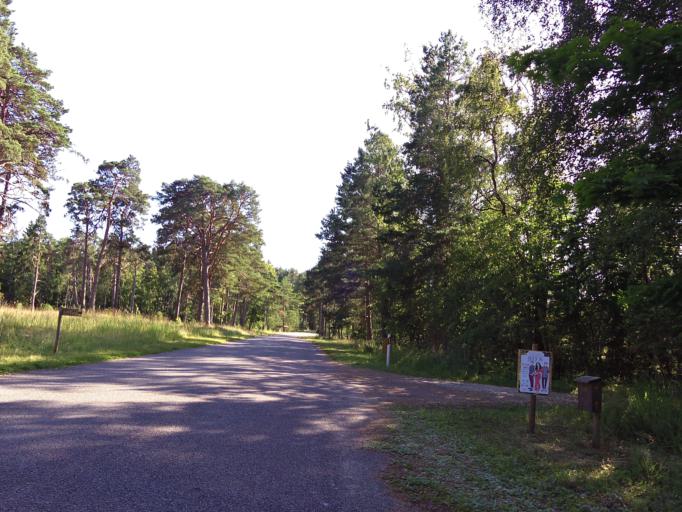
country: EE
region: Hiiumaa
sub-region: Kaerdla linn
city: Kardla
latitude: 58.8932
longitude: 22.2722
